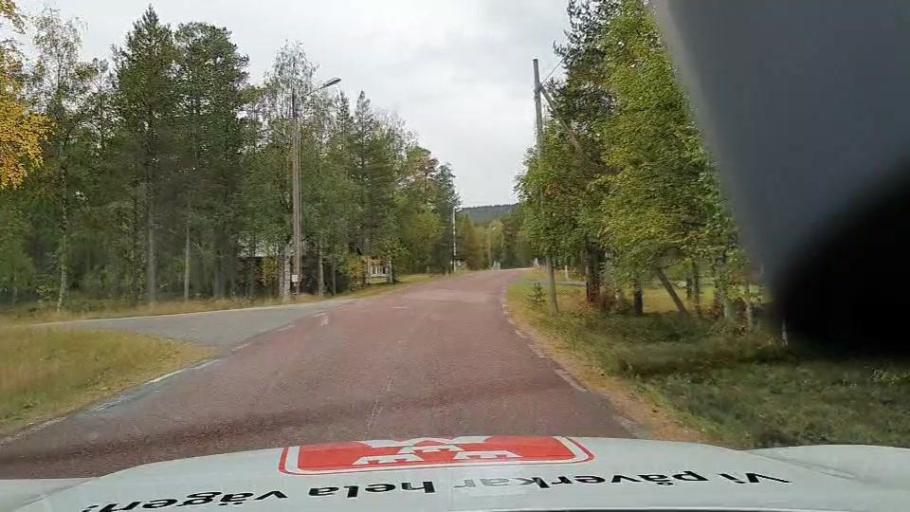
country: NO
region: Hedmark
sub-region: Engerdal
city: Engerdal
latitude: 62.0111
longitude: 12.6661
